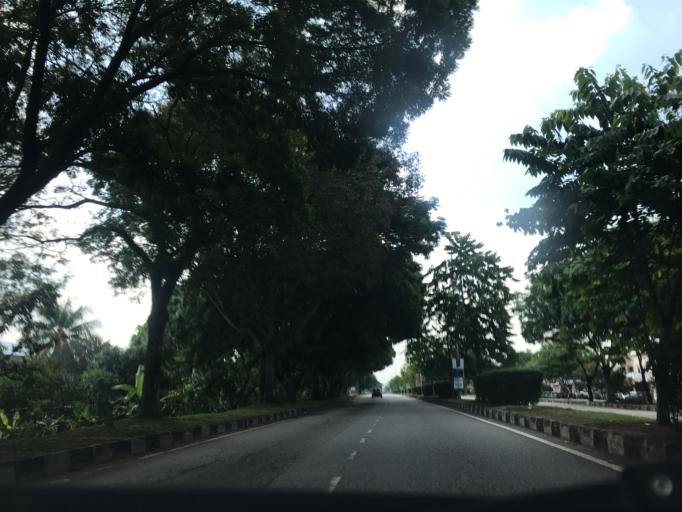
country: MY
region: Perak
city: Ipoh
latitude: 4.6276
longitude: 101.1152
